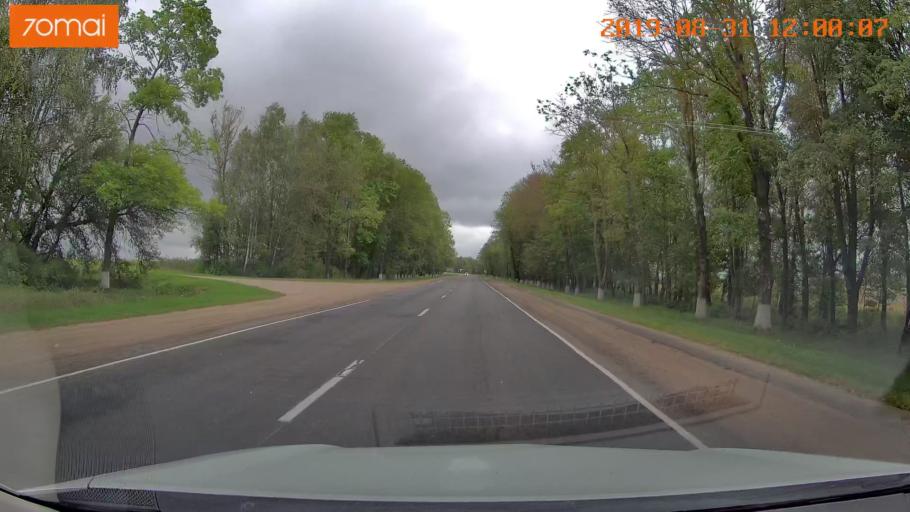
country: BY
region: Mogilev
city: Horad Krychaw
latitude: 53.6769
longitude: 31.6758
